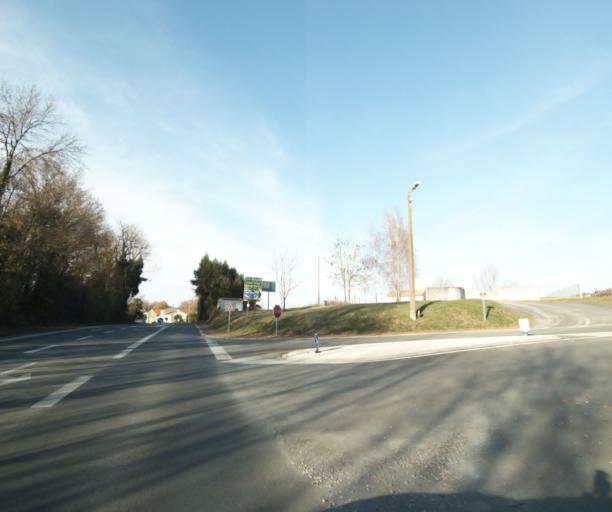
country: FR
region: Poitou-Charentes
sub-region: Departement de la Charente-Maritime
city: Burie
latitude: 45.8006
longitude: -0.4452
